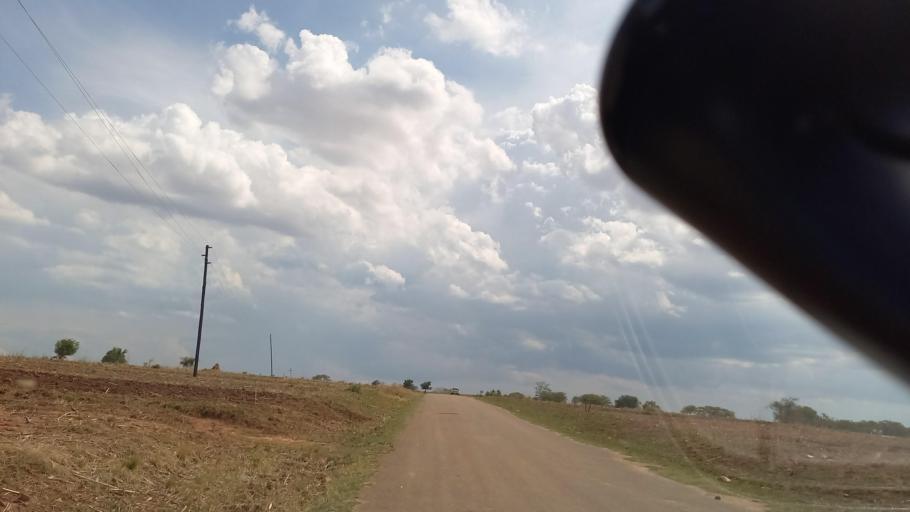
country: ZM
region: Lusaka
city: Kafue
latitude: -16.1826
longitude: 28.0876
